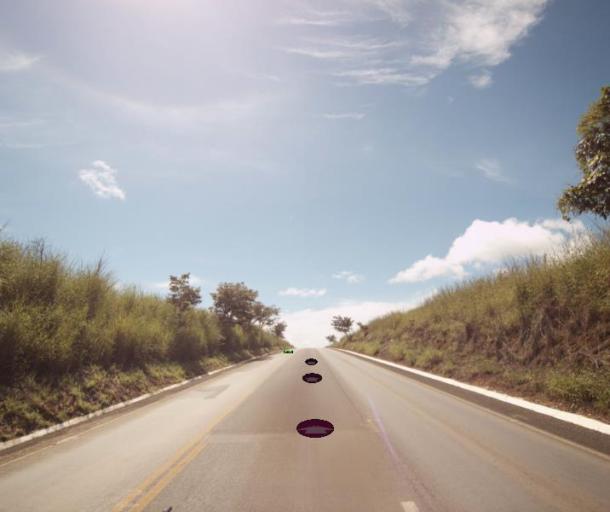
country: BR
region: Goias
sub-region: Padre Bernardo
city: Padre Bernardo
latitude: -15.2136
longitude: -48.4964
